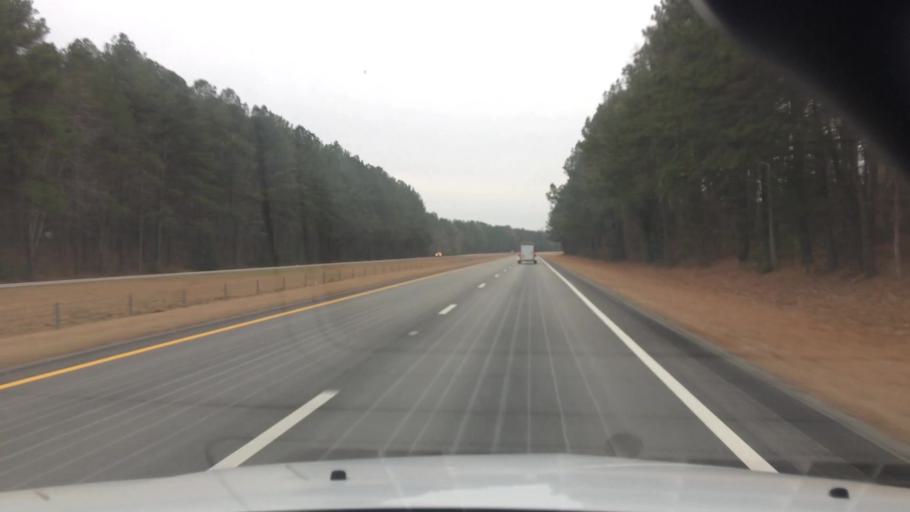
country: US
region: North Carolina
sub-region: Nash County
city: Spring Hope
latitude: 35.8982
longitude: -78.1875
